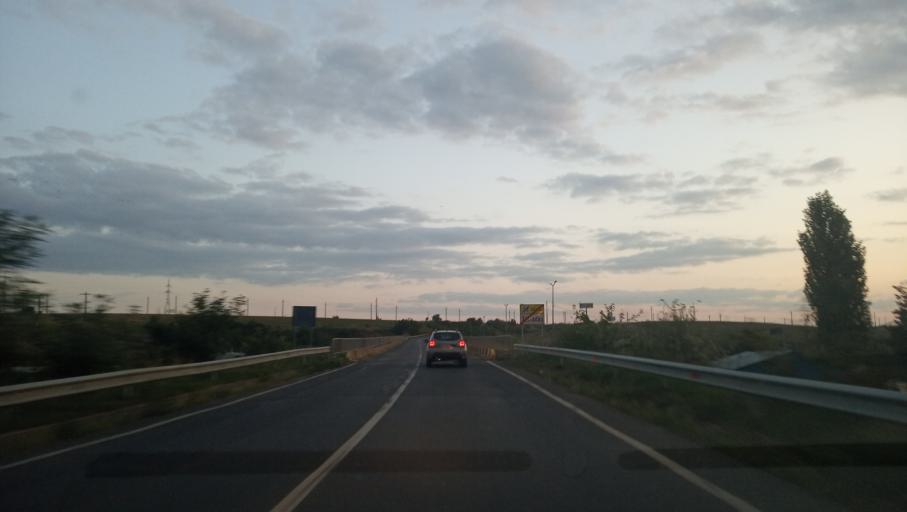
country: RO
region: Calarasi
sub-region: Comuna Tamadau Mare
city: Tamadau Mare
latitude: 44.4635
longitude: 26.5636
